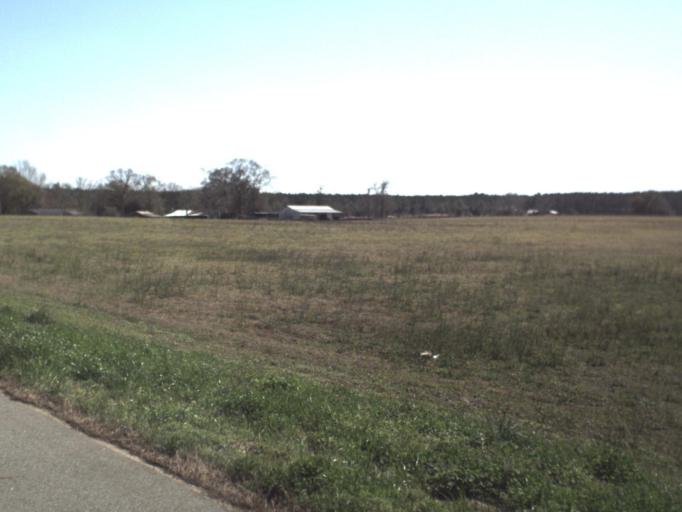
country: US
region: Florida
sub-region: Jackson County
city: Marianna
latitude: 30.8132
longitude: -85.3039
